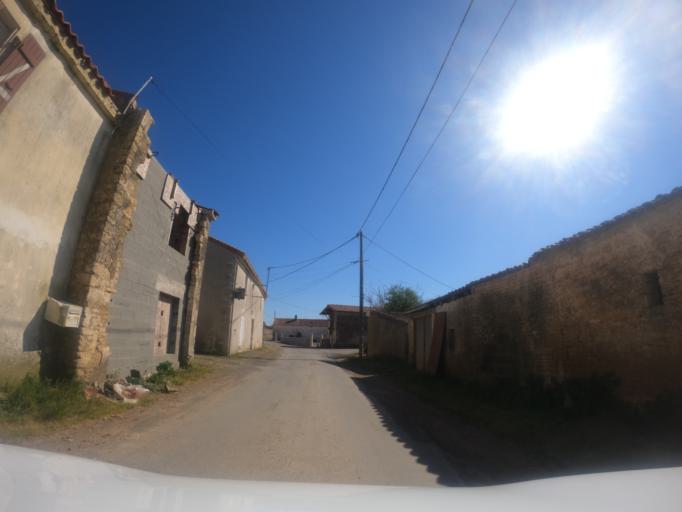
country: FR
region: Pays de la Loire
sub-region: Departement de la Vendee
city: Maillezais
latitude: 46.4106
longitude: -0.7844
